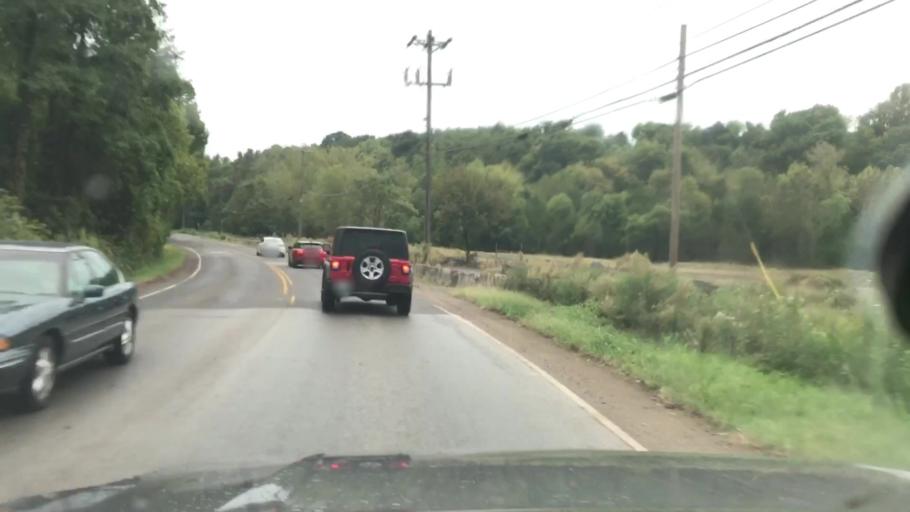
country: US
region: Tennessee
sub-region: Davidson County
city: Lakewood
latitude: 36.1817
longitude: -86.6236
